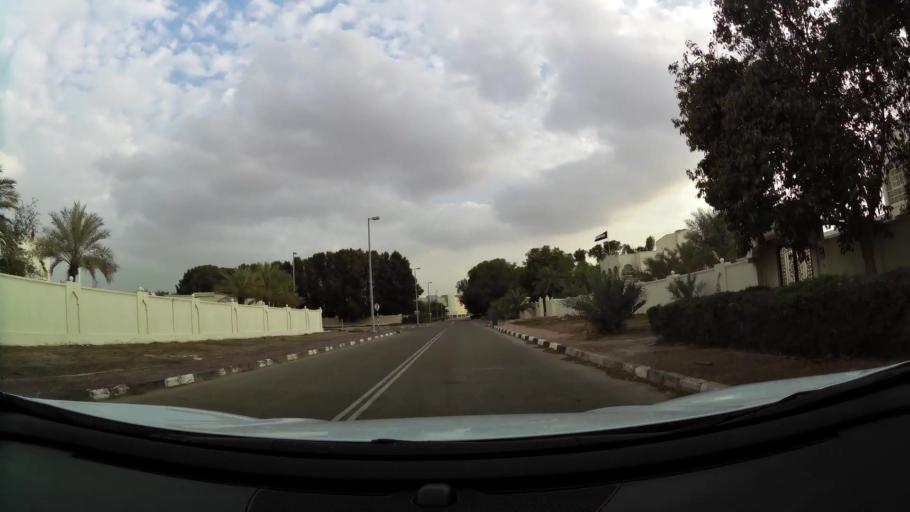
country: AE
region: Abu Dhabi
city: Abu Dhabi
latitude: 24.3821
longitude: 54.5293
